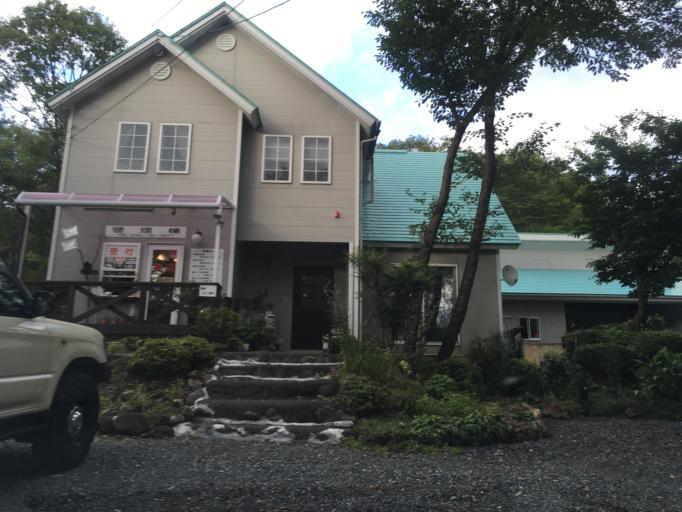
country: JP
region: Iwate
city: Ichinoseki
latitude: 38.9899
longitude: 140.9820
